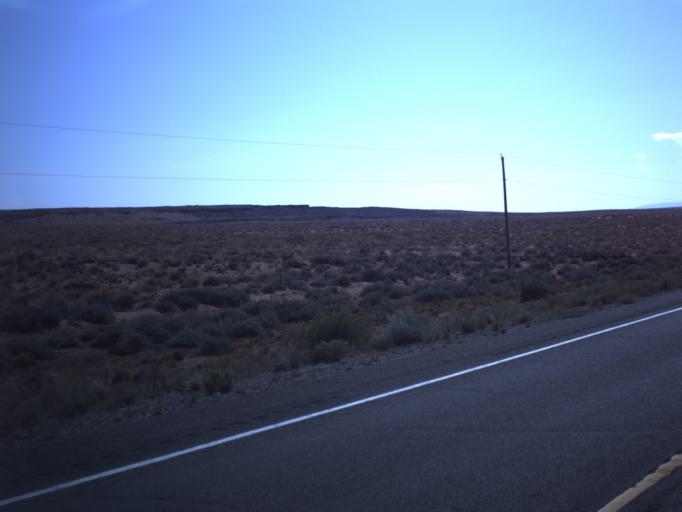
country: US
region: Utah
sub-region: San Juan County
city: Blanding
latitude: 37.1436
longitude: -109.5608
